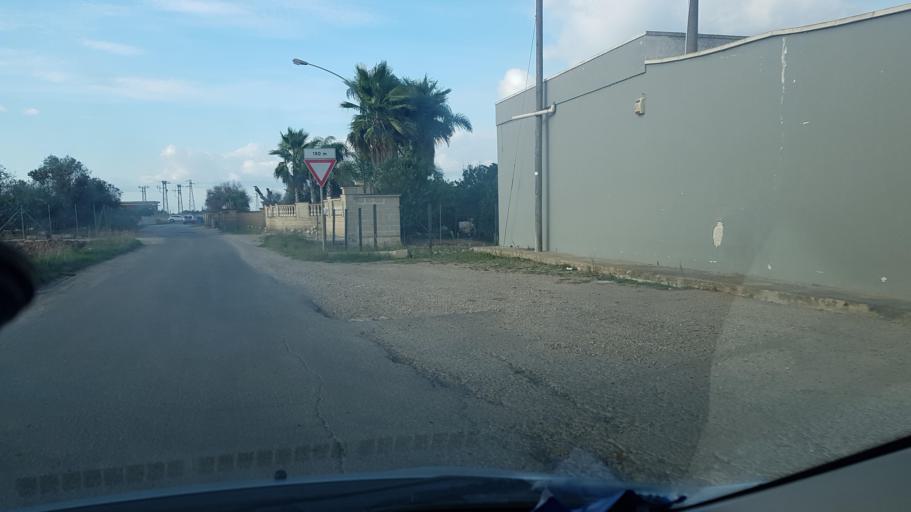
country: IT
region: Apulia
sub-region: Provincia di Lecce
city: Veglie
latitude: 40.3479
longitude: 17.9657
